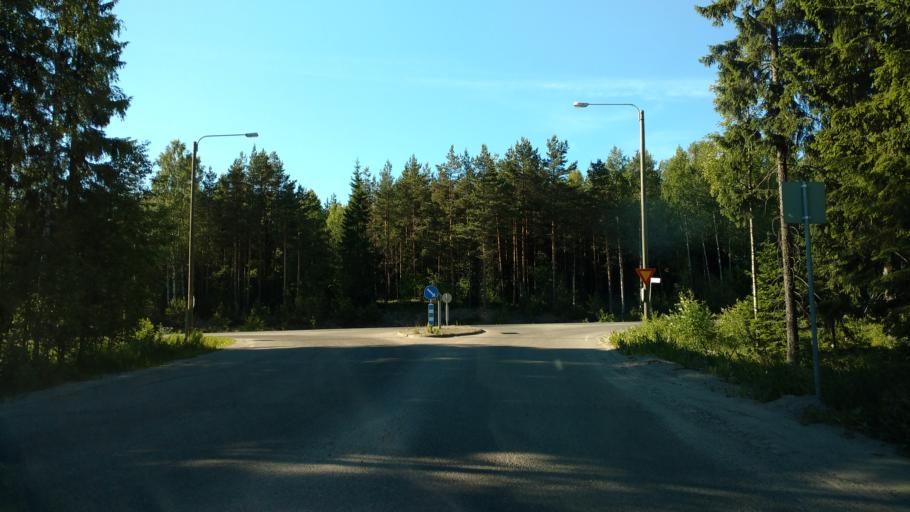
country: FI
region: Varsinais-Suomi
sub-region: Salo
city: Pertteli
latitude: 60.3817
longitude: 23.2225
